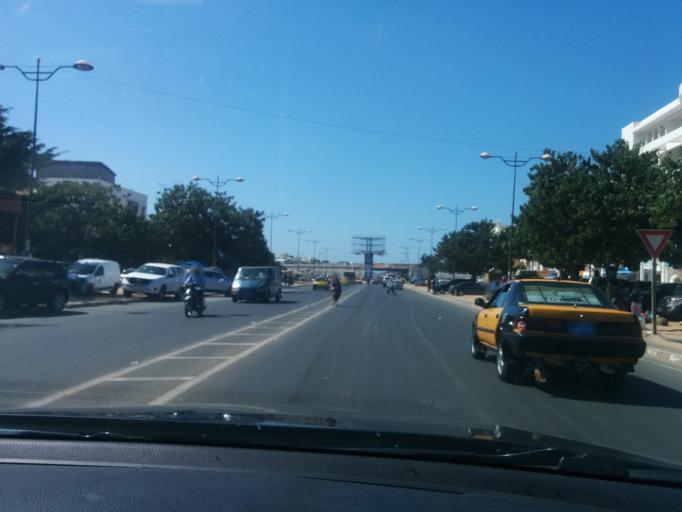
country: SN
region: Dakar
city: Mermoz Boabab
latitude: 14.7164
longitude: -17.4695
